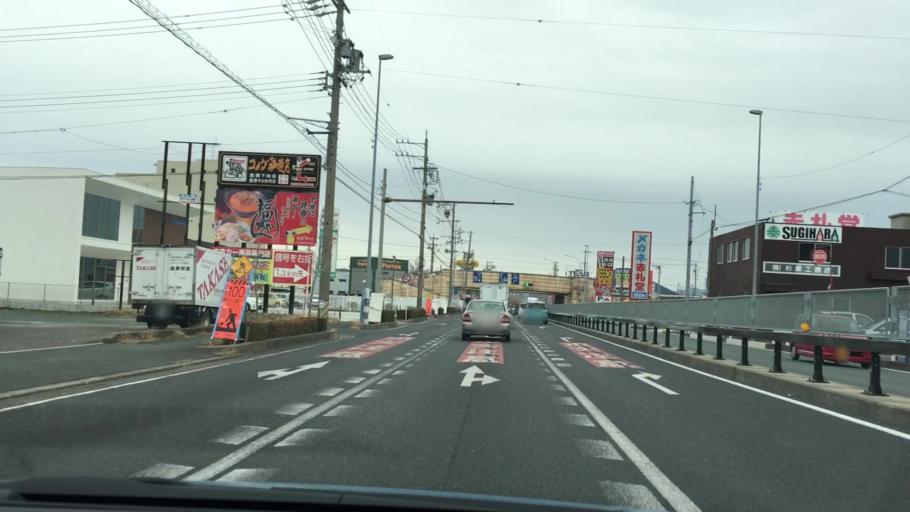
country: JP
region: Aichi
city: Toyohashi
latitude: 34.7752
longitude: 137.3884
